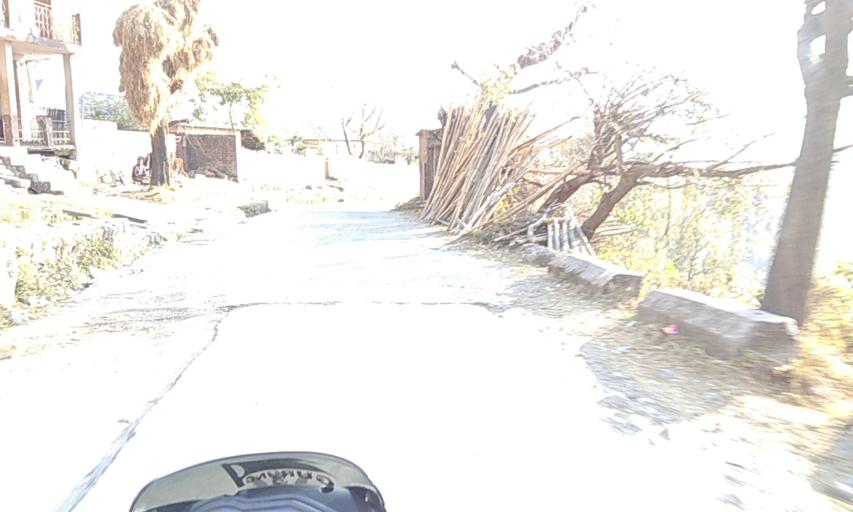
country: IN
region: Himachal Pradesh
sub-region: Kangra
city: Palampur
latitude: 32.1313
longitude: 76.5360
